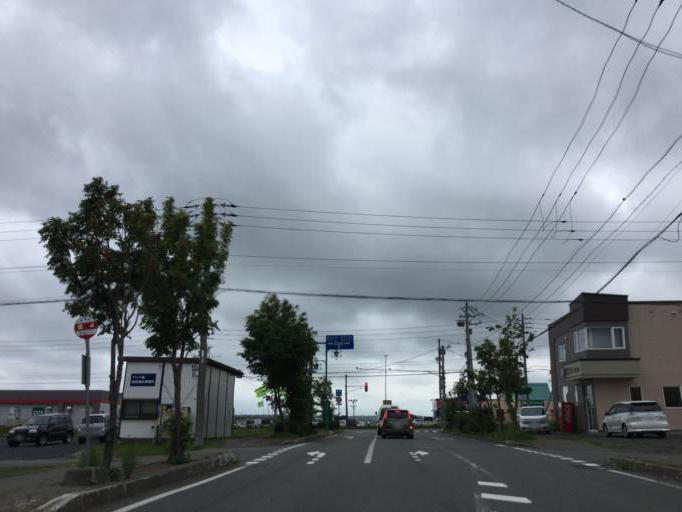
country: JP
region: Hokkaido
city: Wakkanai
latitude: 45.3871
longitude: 141.6996
